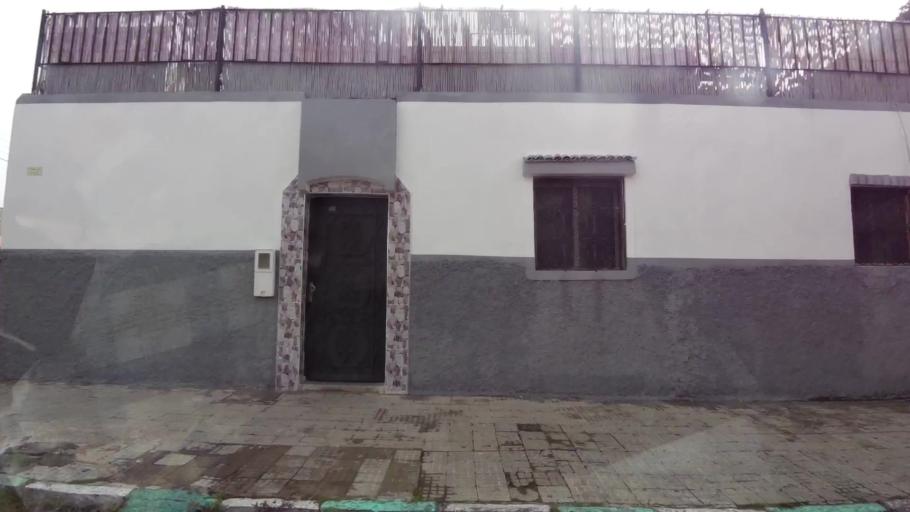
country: MA
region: Grand Casablanca
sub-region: Casablanca
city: Casablanca
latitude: 33.5647
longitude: -7.6709
